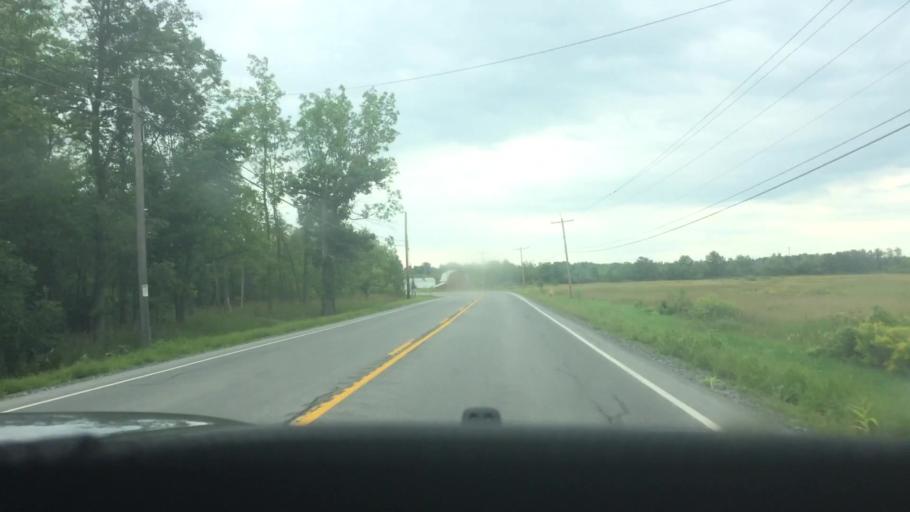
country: US
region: New York
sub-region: St. Lawrence County
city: Ogdensburg
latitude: 44.6290
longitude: -75.4215
